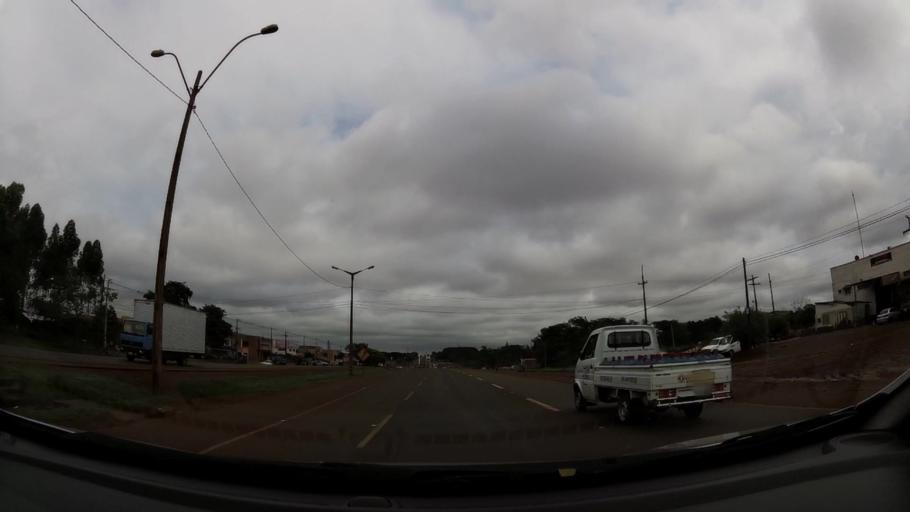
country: PY
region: Alto Parana
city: Ciudad del Este
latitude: -25.4941
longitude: -54.7089
